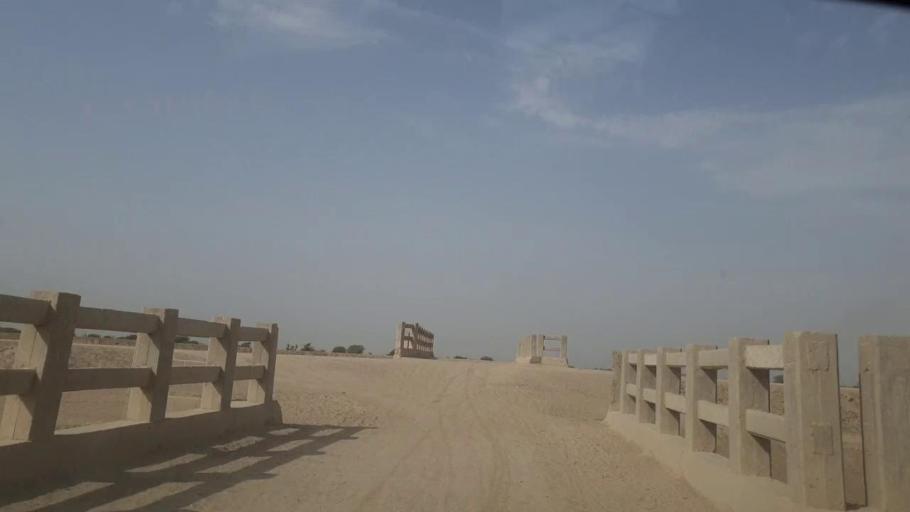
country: PK
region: Sindh
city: Nabisar
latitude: 25.0385
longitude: 69.4975
